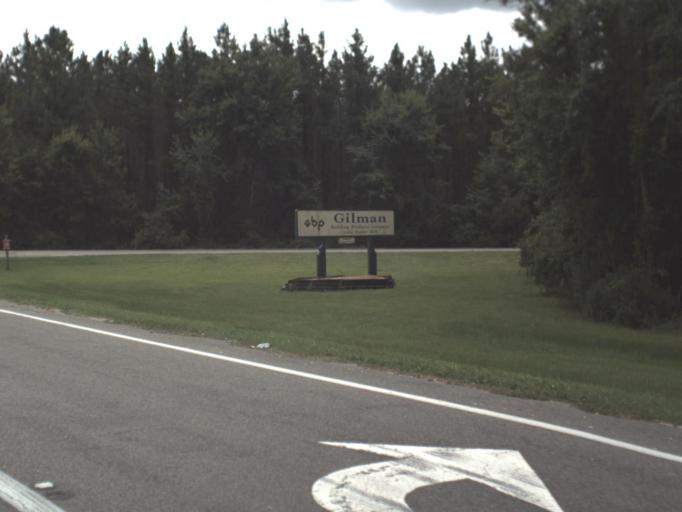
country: US
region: Florida
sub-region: Union County
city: Lake Butler
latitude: 30.0132
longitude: -82.3045
